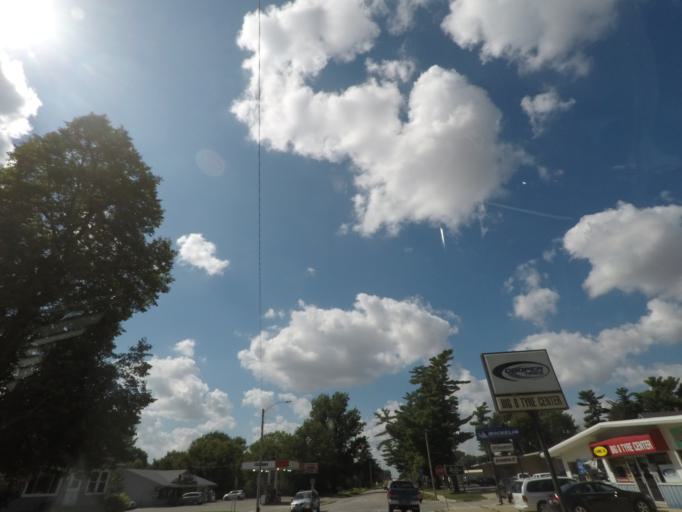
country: US
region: Iowa
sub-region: Story County
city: Nevada
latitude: 42.0227
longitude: -93.4572
